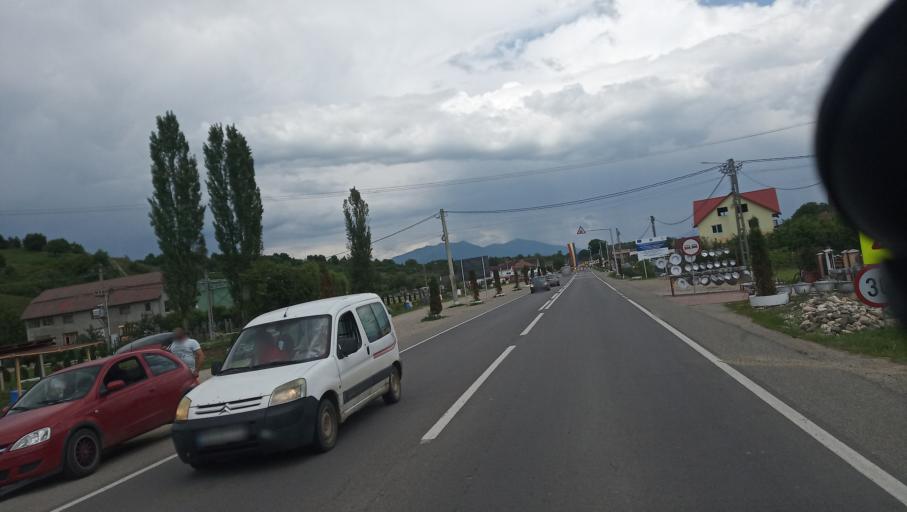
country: RO
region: Bistrita-Nasaud
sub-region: Comuna Livezile
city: Livezile
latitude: 47.1793
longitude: 24.5550
